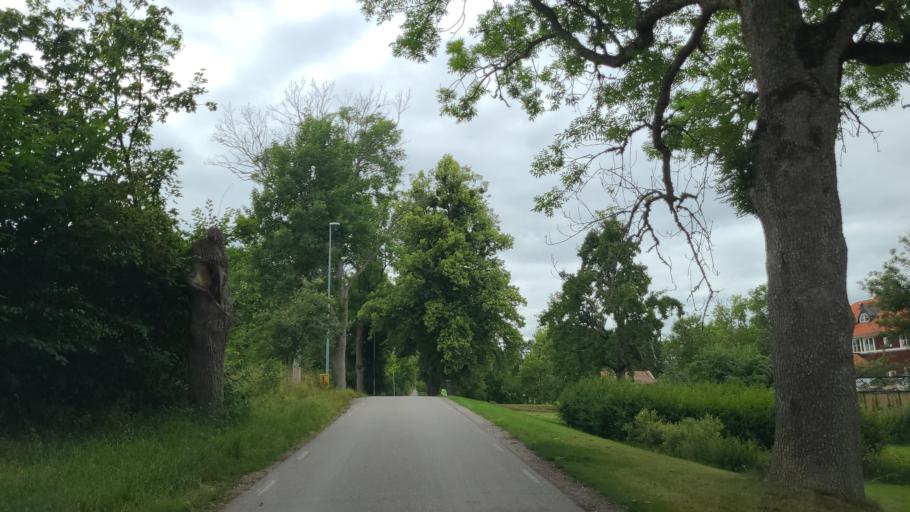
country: SE
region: Stockholm
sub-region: Upplands-Bro Kommun
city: Bro
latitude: 59.5086
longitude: 17.5681
